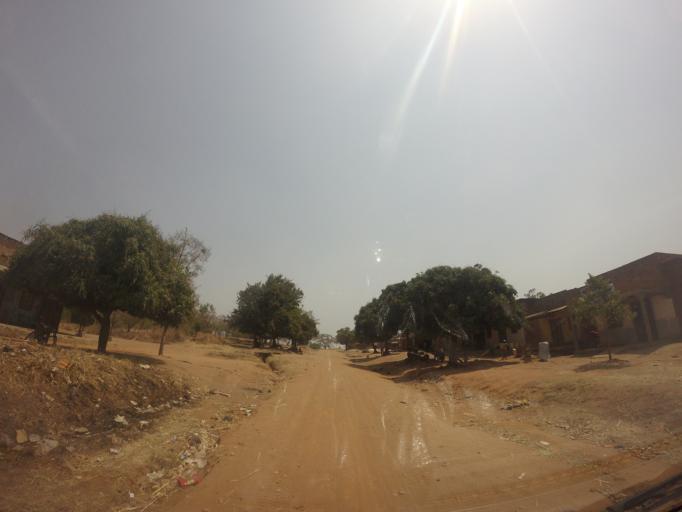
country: UG
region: Northern Region
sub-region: Arua District
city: Arua
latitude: 2.9157
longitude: 31.0259
